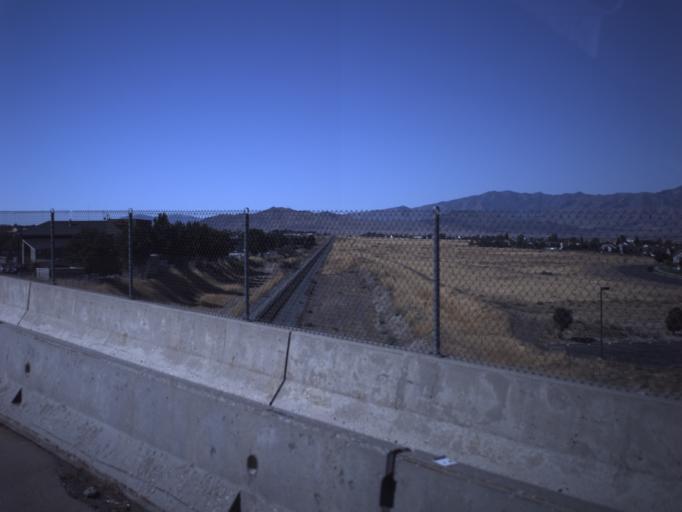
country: US
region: Utah
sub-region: Tooele County
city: Tooele
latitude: 40.5623
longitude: -112.2964
